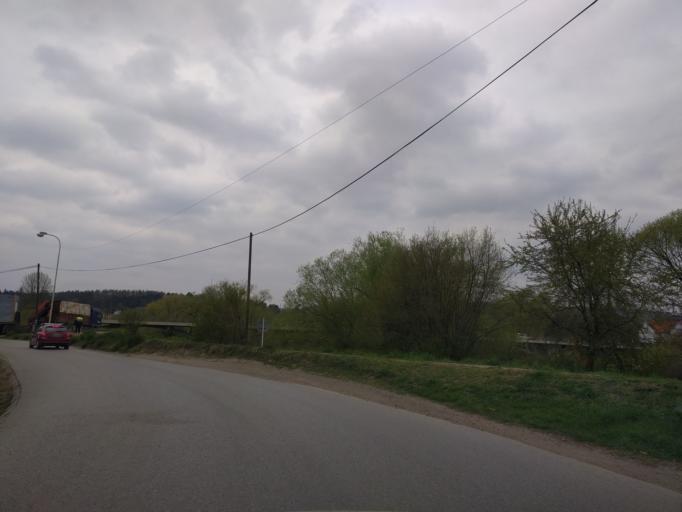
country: CZ
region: Central Bohemia
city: Revnice
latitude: 49.9180
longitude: 14.2488
